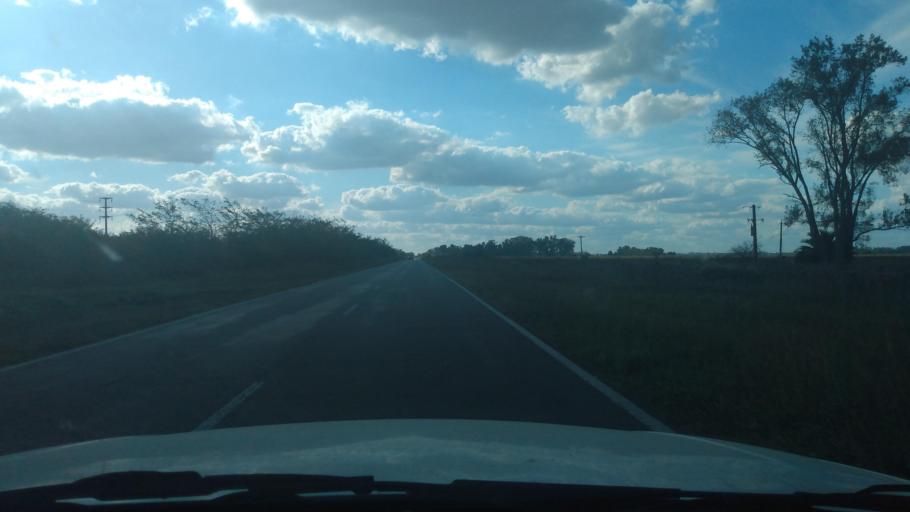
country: AR
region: Buenos Aires
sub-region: Partido de Mercedes
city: Mercedes
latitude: -34.7696
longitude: -59.3718
